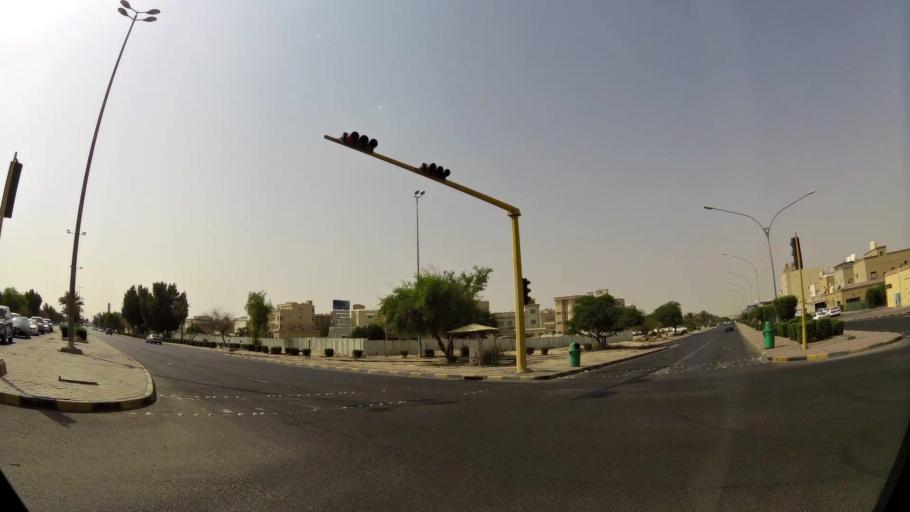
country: KW
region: Muhafazat al Jahra'
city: Al Jahra'
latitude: 29.3318
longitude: 47.7061
